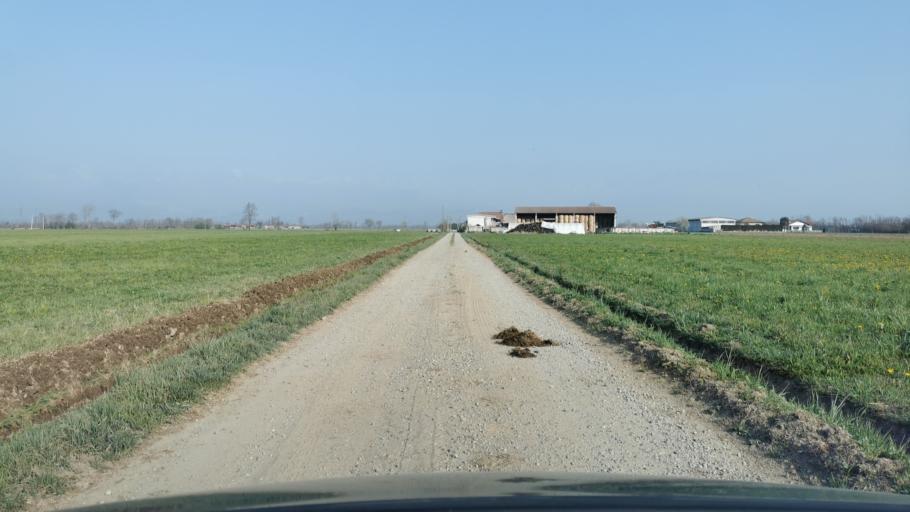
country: IT
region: Piedmont
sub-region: Provincia di Torino
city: Rivarossa
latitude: 45.2646
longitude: 7.7298
